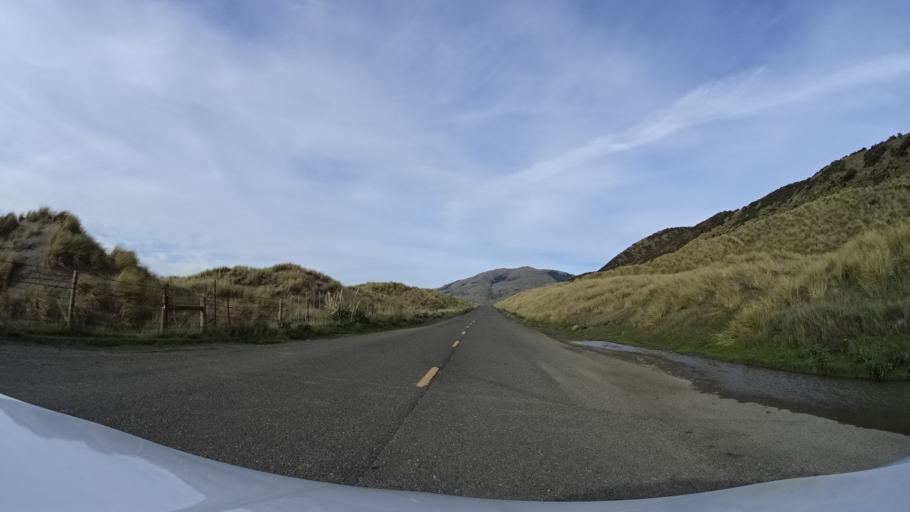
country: US
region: California
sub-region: Humboldt County
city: Ferndale
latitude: 40.3533
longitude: -124.3611
